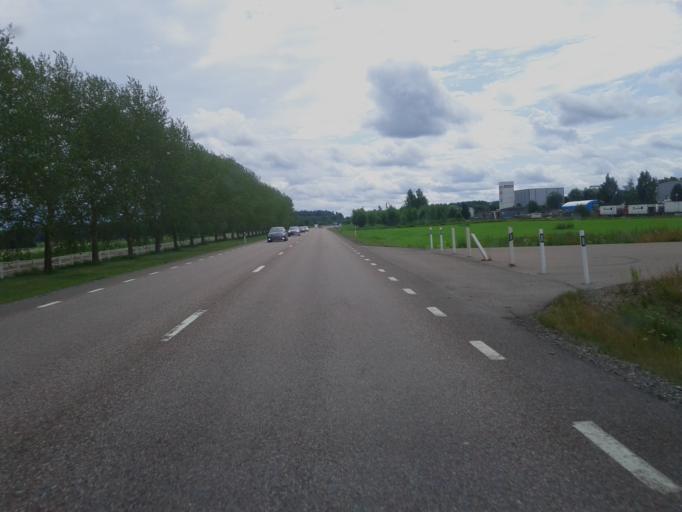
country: SE
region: Dalarna
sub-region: Borlange Kommun
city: Borlaenge
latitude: 60.4447
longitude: 15.4997
